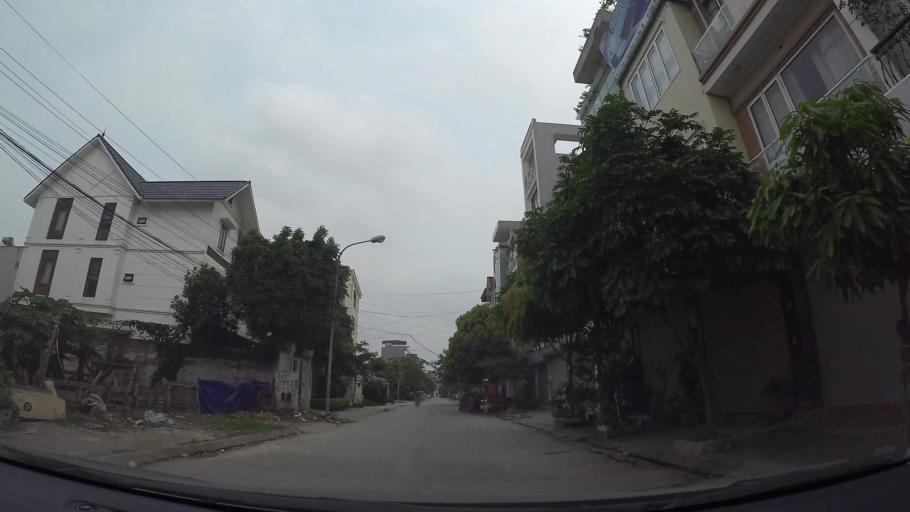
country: VN
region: Ha Noi
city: Trau Quy
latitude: 21.0544
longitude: 105.9041
